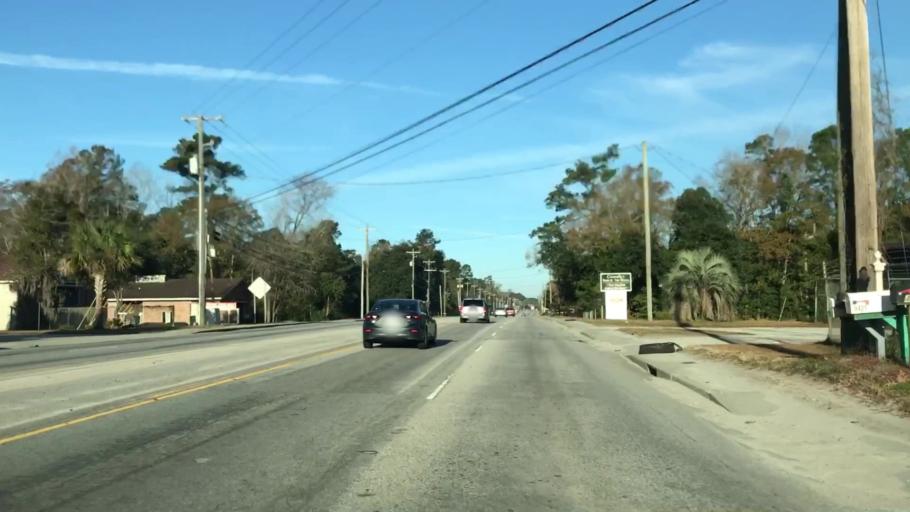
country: US
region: South Carolina
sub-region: Berkeley County
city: Ladson
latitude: 32.9827
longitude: -80.0894
